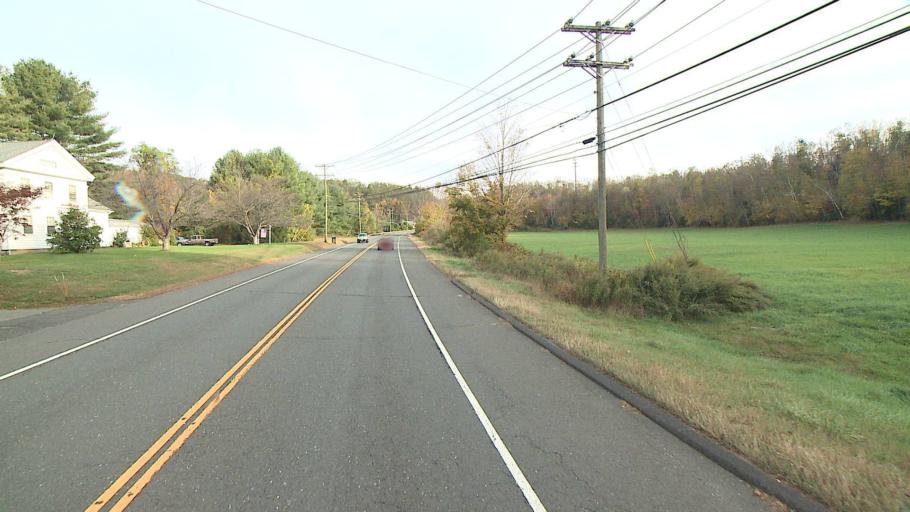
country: US
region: Connecticut
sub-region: Litchfield County
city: New Hartford Center
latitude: 41.8534
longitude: -72.9517
